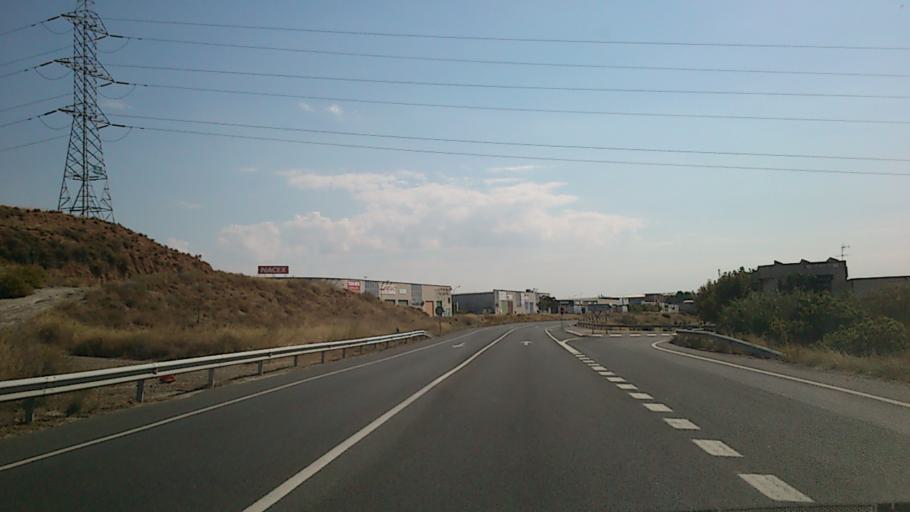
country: ES
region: Aragon
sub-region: Provincia de Zaragoza
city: Puebla de Alfinden
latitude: 41.6425
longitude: -0.7728
